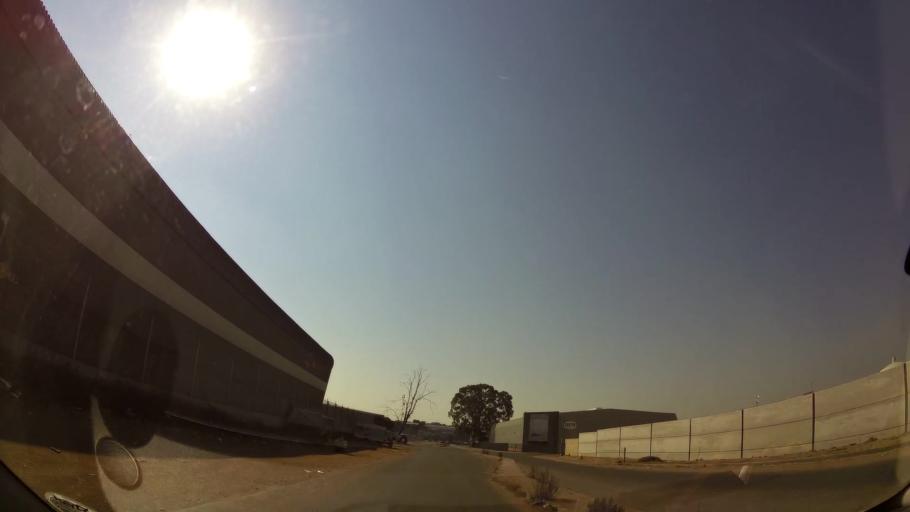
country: ZA
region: Gauteng
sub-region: Ekurhuleni Metropolitan Municipality
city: Boksburg
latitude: -26.1602
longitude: 28.2169
